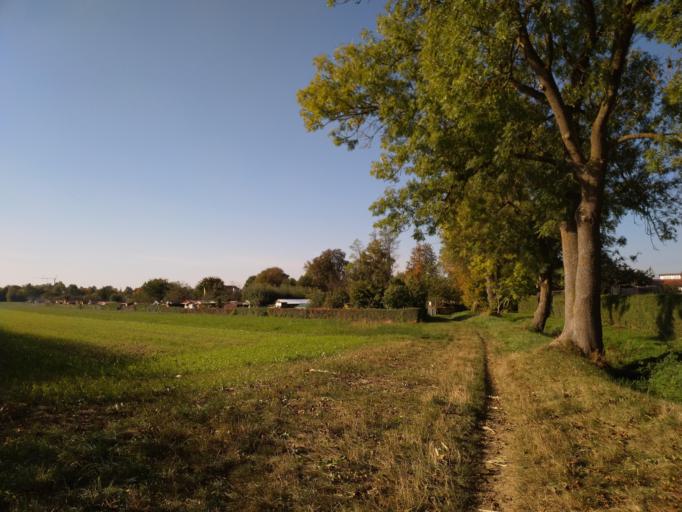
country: DE
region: Bavaria
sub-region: Swabia
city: Guenzburg
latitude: 48.4461
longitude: 10.2964
